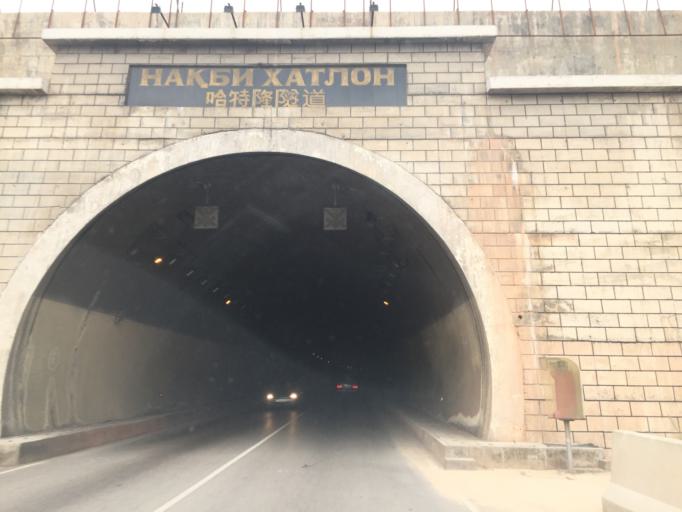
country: TJ
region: Khatlon
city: Norak
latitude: 38.4869
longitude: 69.1768
